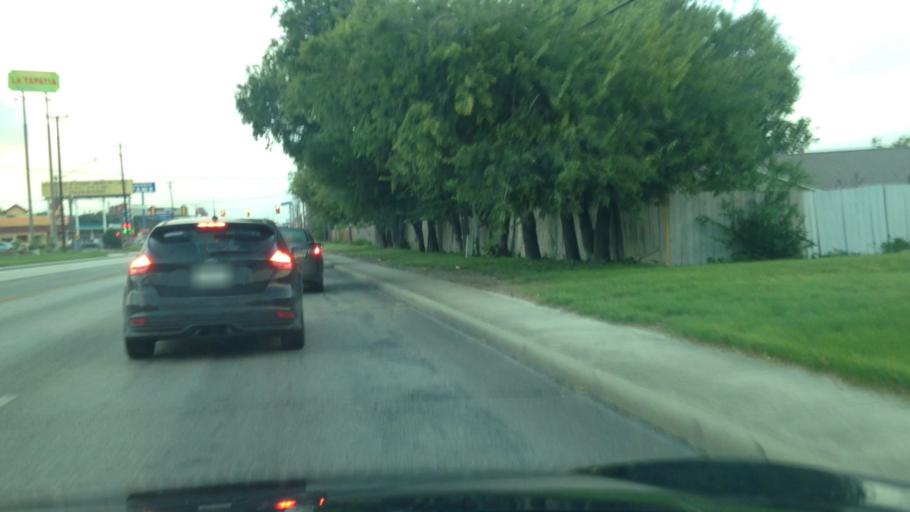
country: US
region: Texas
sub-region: Bexar County
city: Windcrest
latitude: 29.5218
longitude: -98.4111
